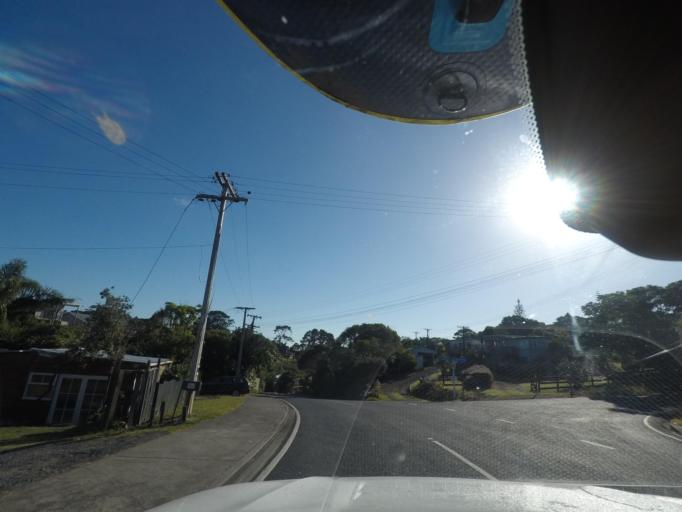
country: NZ
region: Auckland
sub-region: Auckland
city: Parakai
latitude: -36.5703
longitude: 174.3759
